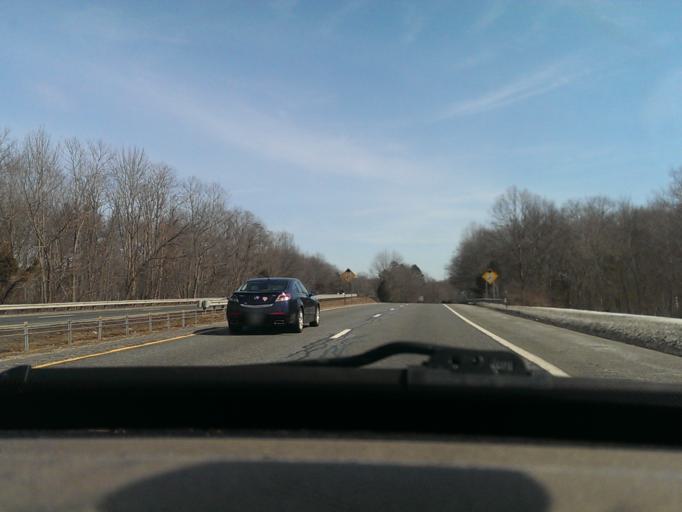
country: US
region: Rhode Island
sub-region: Providence County
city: Woonsocket
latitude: 41.9711
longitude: -71.5127
